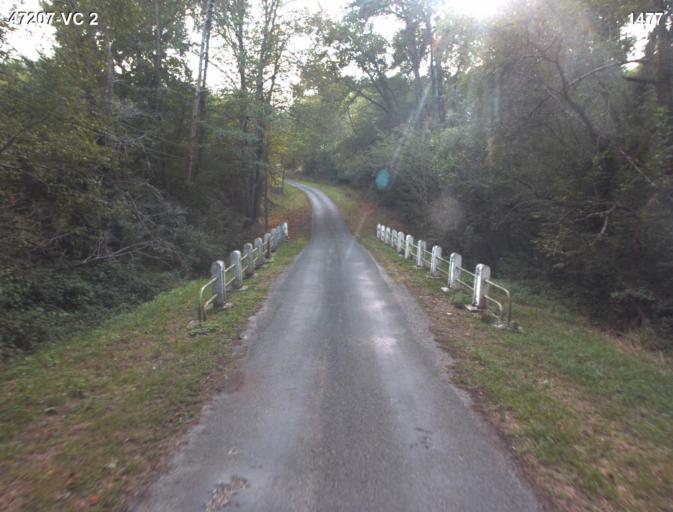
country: FR
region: Aquitaine
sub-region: Departement du Lot-et-Garonne
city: Barbaste
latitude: 44.1896
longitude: 0.2291
